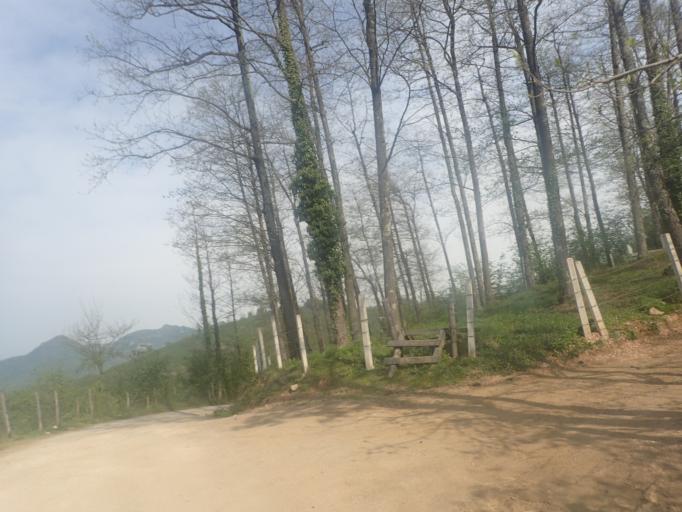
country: TR
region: Ordu
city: Catalpinar
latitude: 40.8826
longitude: 37.4867
